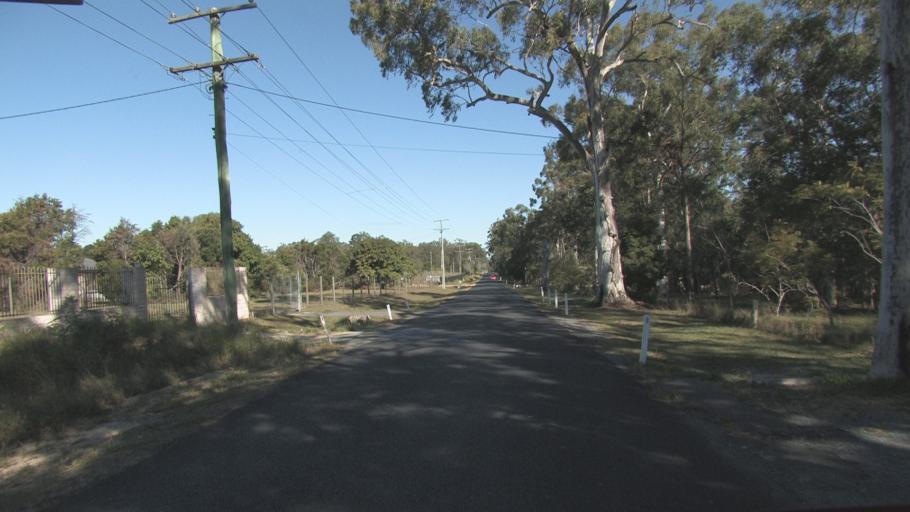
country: AU
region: Queensland
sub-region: Logan
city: Logan Reserve
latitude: -27.7232
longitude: 153.0736
